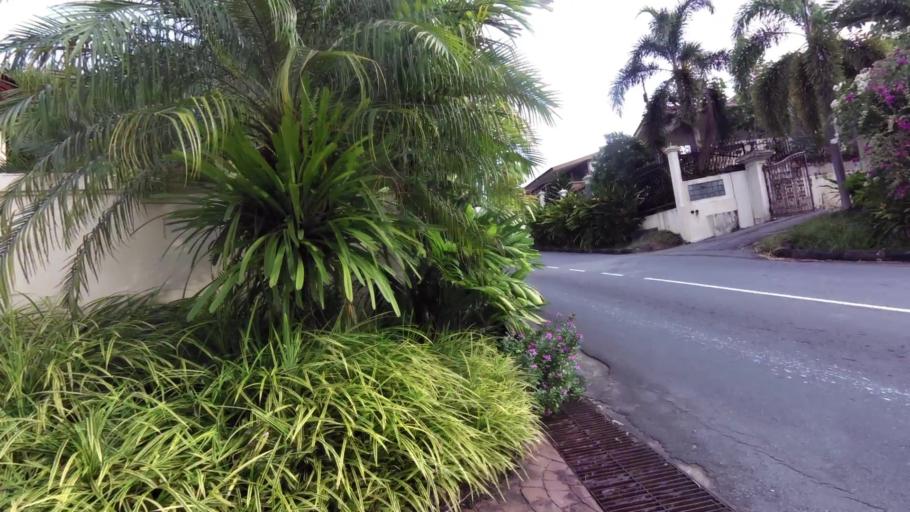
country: BN
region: Brunei and Muara
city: Bandar Seri Begawan
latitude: 4.9022
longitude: 114.8974
